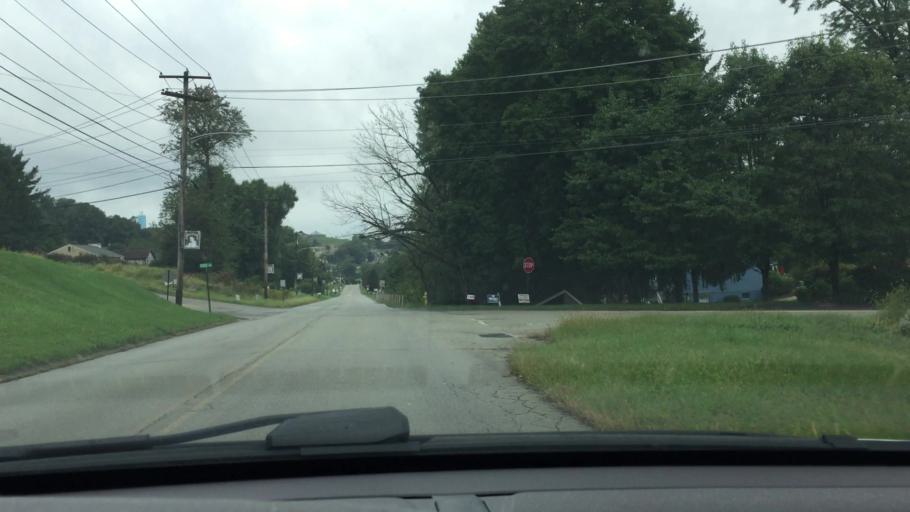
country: US
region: Pennsylvania
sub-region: Westmoreland County
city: North Belle Vernon
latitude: 40.1441
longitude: -79.8692
